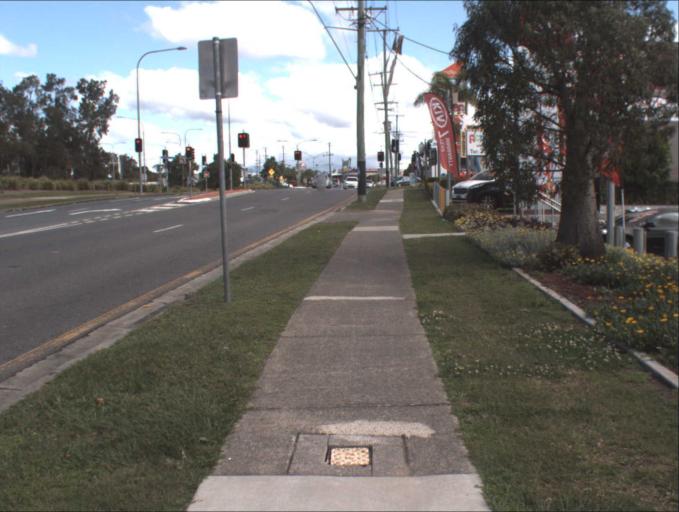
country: AU
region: Queensland
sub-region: Logan
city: Park Ridge South
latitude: -27.6668
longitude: 153.0330
